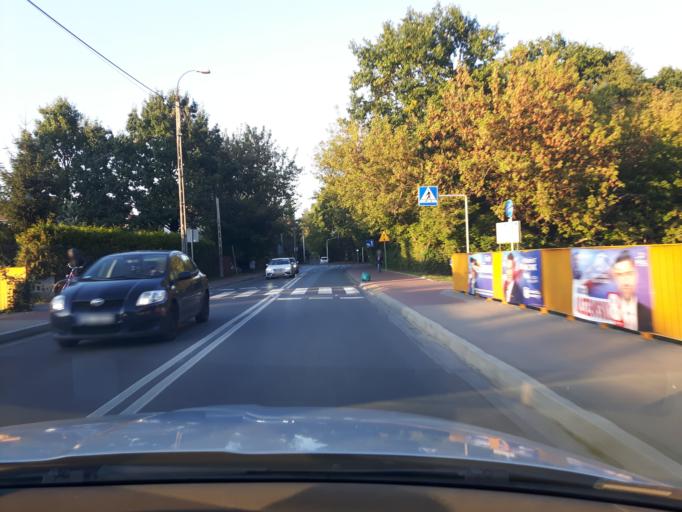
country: PL
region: Masovian Voivodeship
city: Zielonka
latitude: 52.3130
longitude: 21.1546
